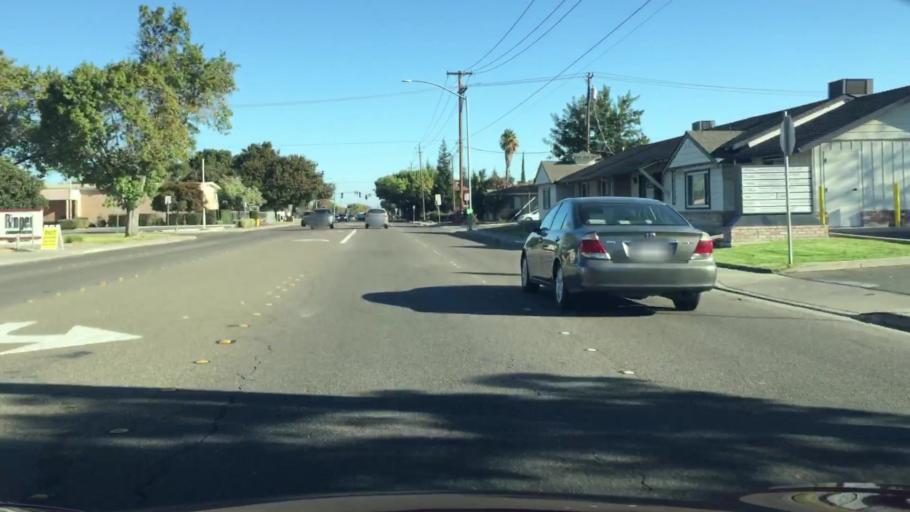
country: US
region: California
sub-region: San Joaquin County
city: Tracy
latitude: 37.7402
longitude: -121.4361
